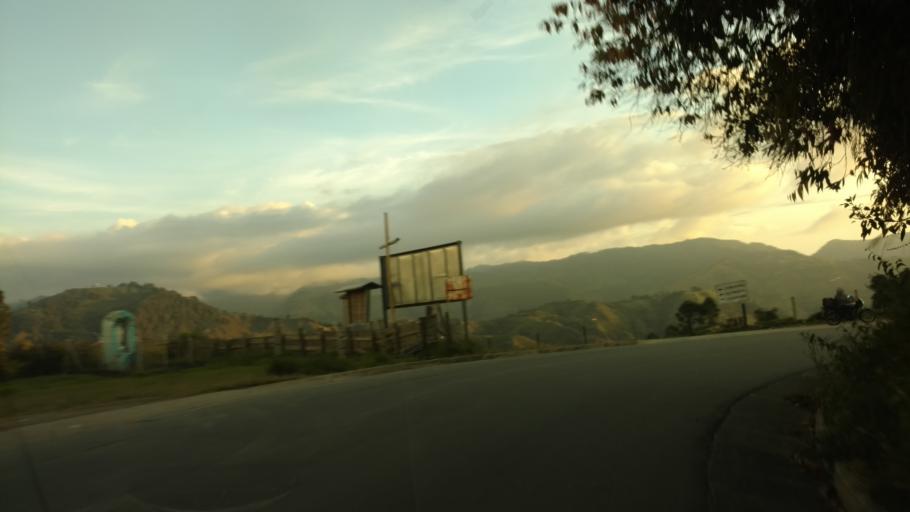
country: CO
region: Caldas
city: Aranzazu
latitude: 5.2843
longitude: -75.4866
